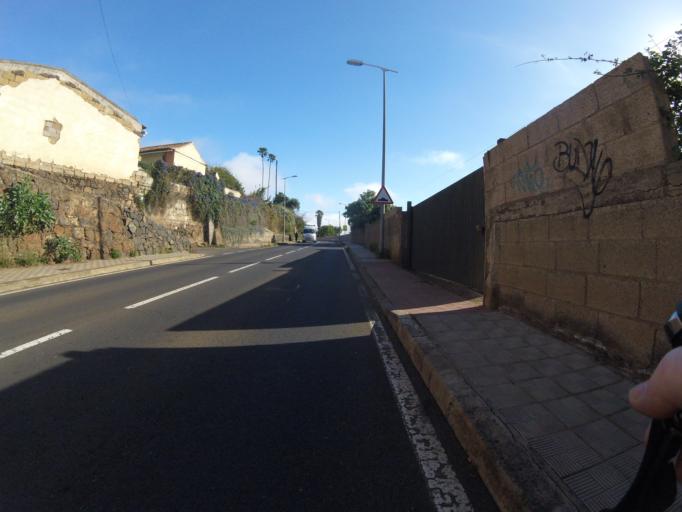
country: ES
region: Canary Islands
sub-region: Provincia de Santa Cruz de Tenerife
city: La Laguna
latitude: 28.4691
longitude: -16.3170
